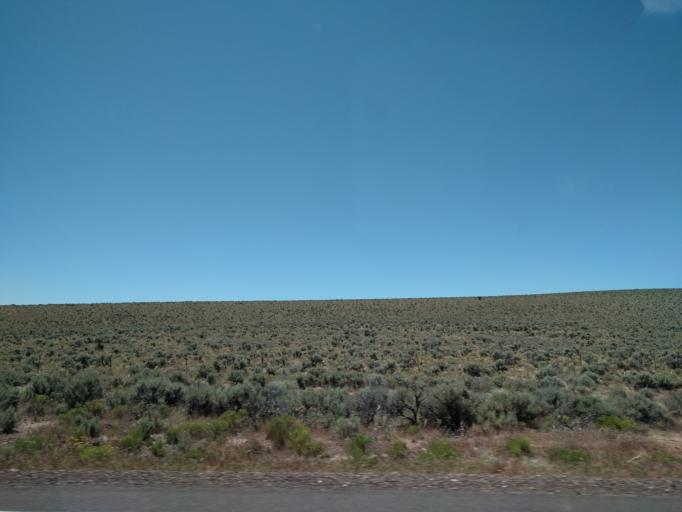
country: US
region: Oregon
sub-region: Harney County
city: Hines
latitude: 43.5837
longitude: -119.9581
